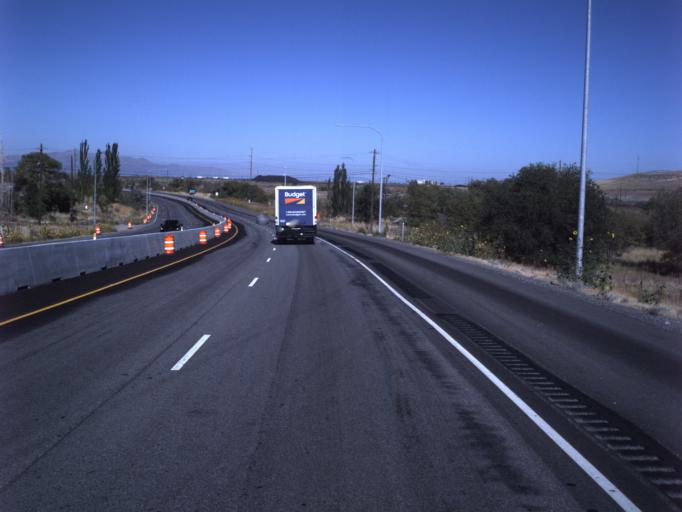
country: US
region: Utah
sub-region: Salt Lake County
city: Magna
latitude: 40.7252
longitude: -112.1611
